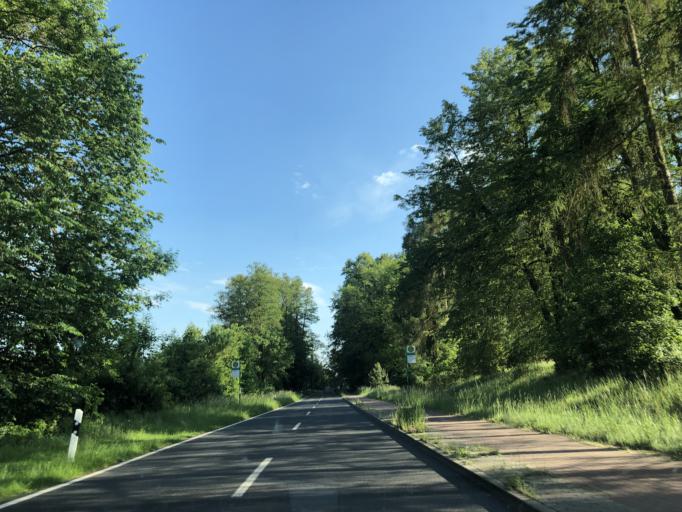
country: DE
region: Brandenburg
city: Joachimsthal
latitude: 52.9488
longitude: 13.7186
